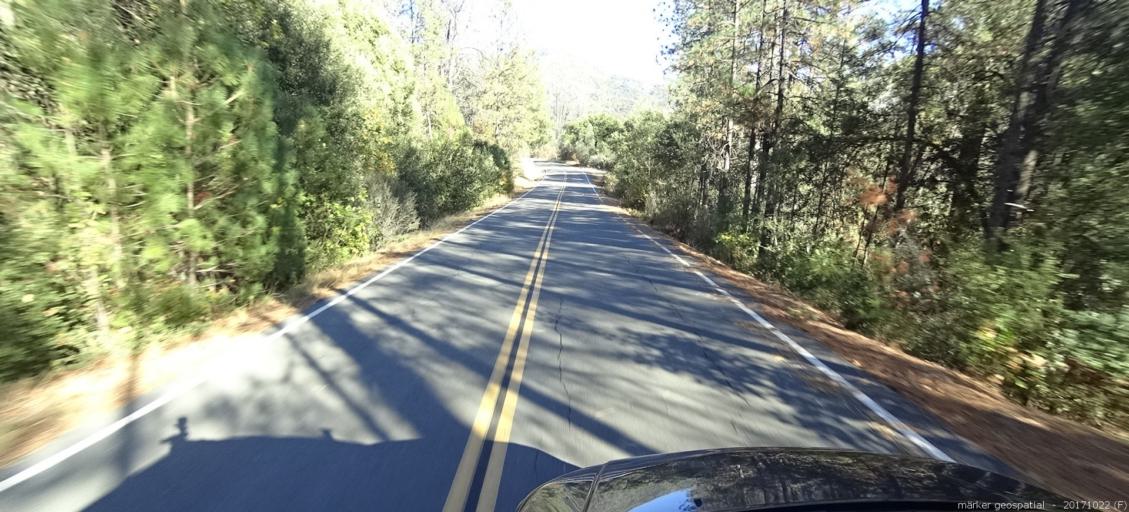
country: US
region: California
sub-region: Shasta County
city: Bella Vista
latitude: 40.8753
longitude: -122.2368
